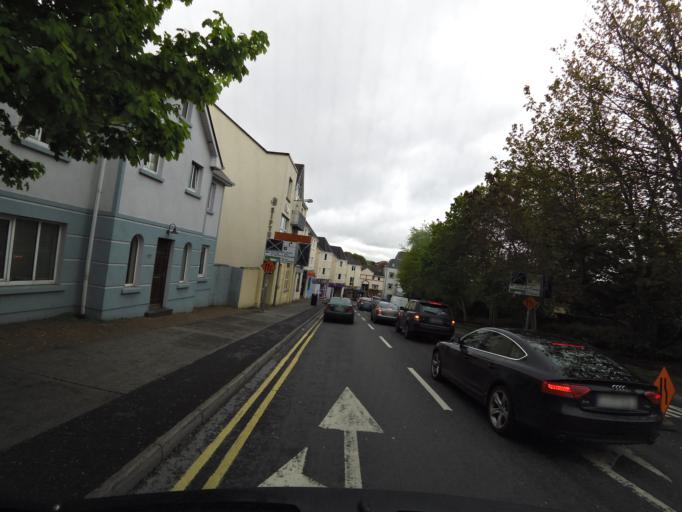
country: IE
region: Connaught
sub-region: County Galway
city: Gaillimh
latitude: 53.2764
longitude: -9.0473
